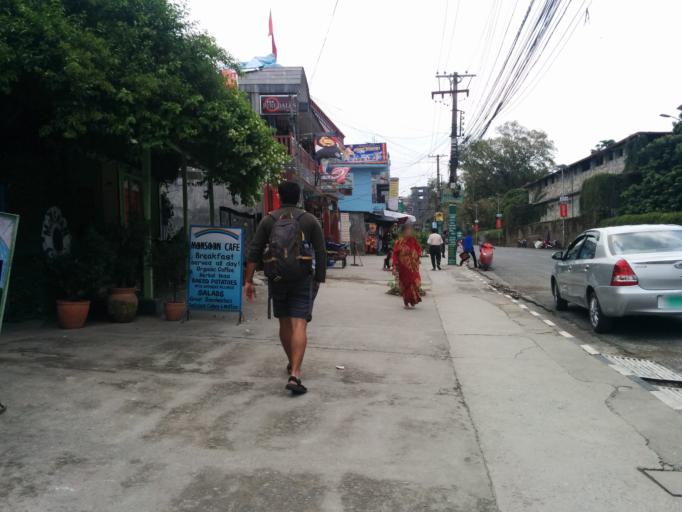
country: NP
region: Western Region
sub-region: Gandaki Zone
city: Pokhara
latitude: 28.2070
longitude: 83.9581
